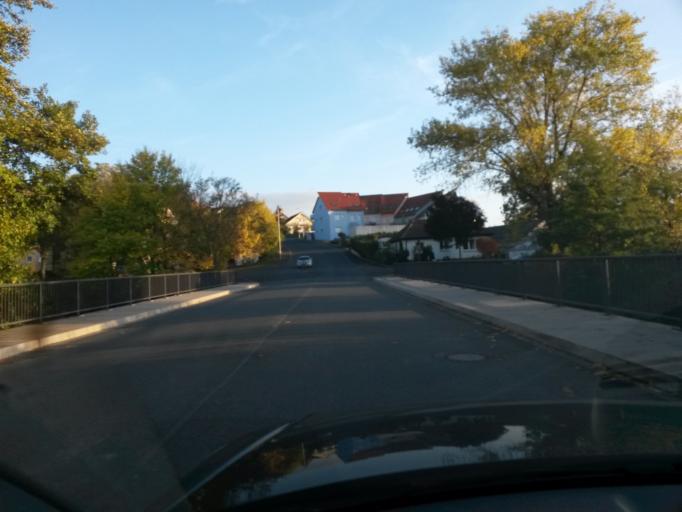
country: DE
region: Bavaria
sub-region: Regierungsbezirk Unterfranken
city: Rimpar
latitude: 49.8505
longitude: 9.9579
